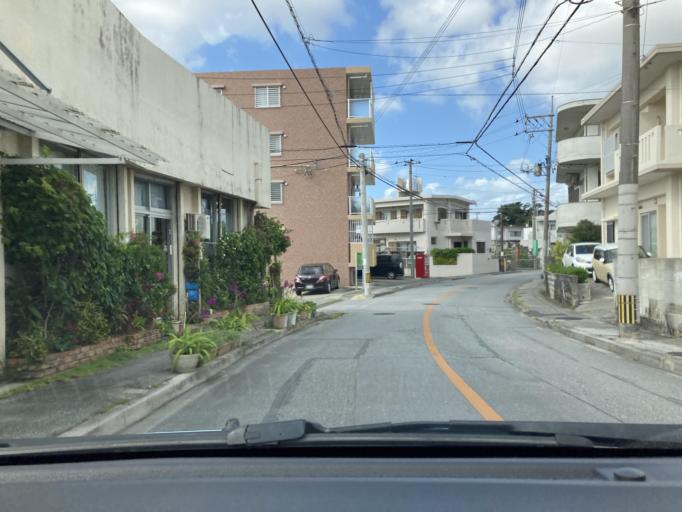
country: JP
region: Okinawa
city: Naha-shi
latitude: 26.2062
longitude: 127.7101
